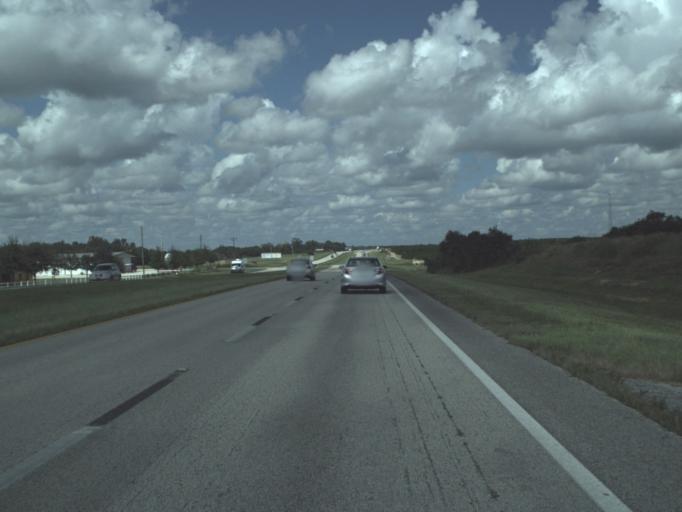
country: US
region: Florida
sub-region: Highlands County
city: Lake Placid
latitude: 27.3258
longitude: -81.3747
